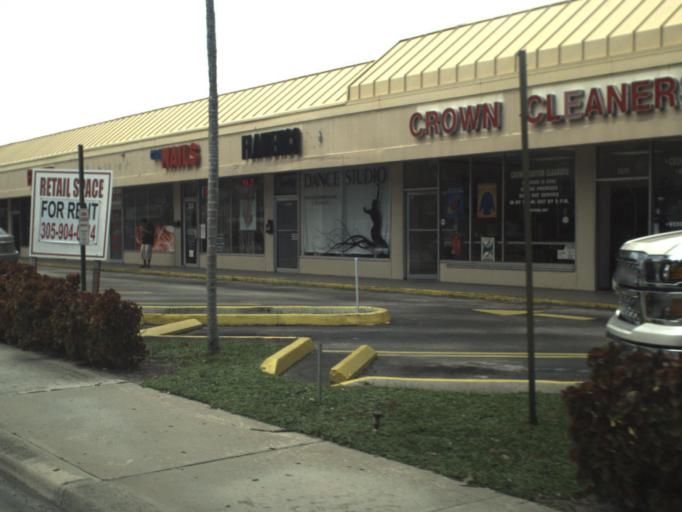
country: US
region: Florida
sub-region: Miami-Dade County
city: North Miami Beach
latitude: 25.9262
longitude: -80.1592
